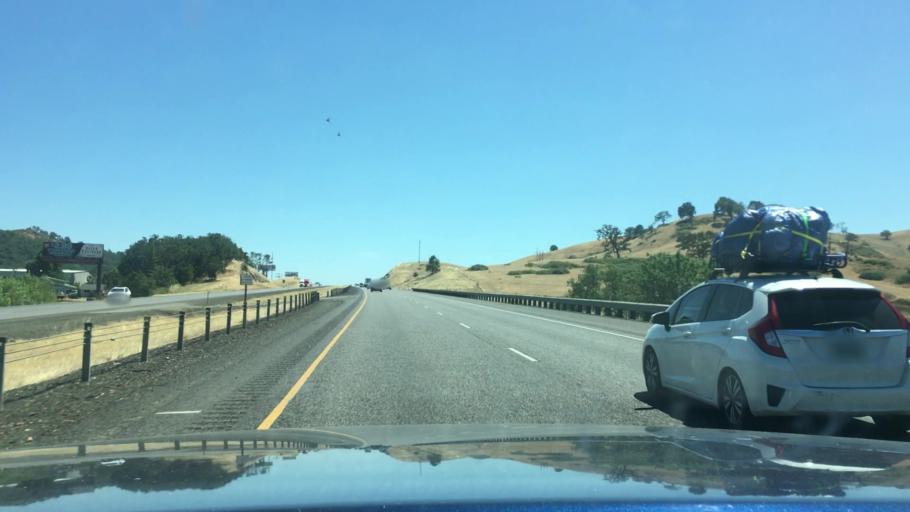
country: US
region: Oregon
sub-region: Douglas County
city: Roseburg North
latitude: 43.3150
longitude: -123.3476
